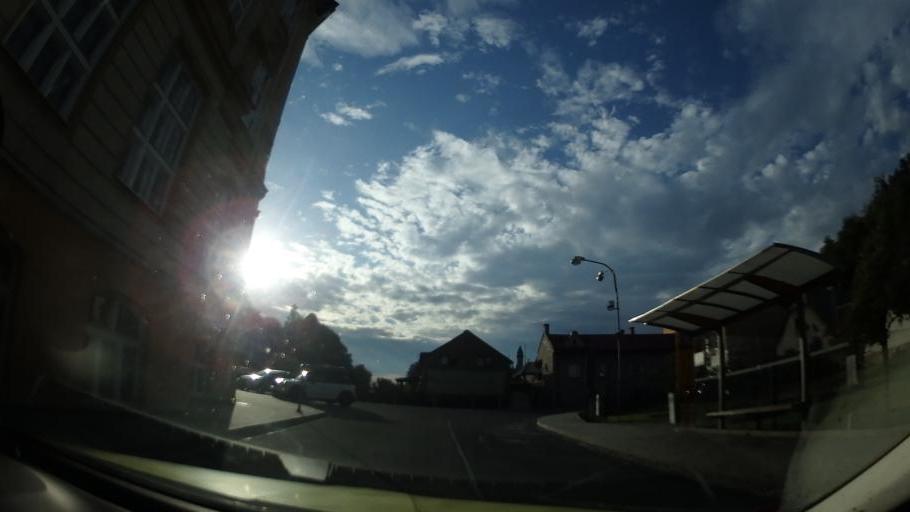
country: CZ
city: Stramberk
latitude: 49.5872
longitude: 18.1224
